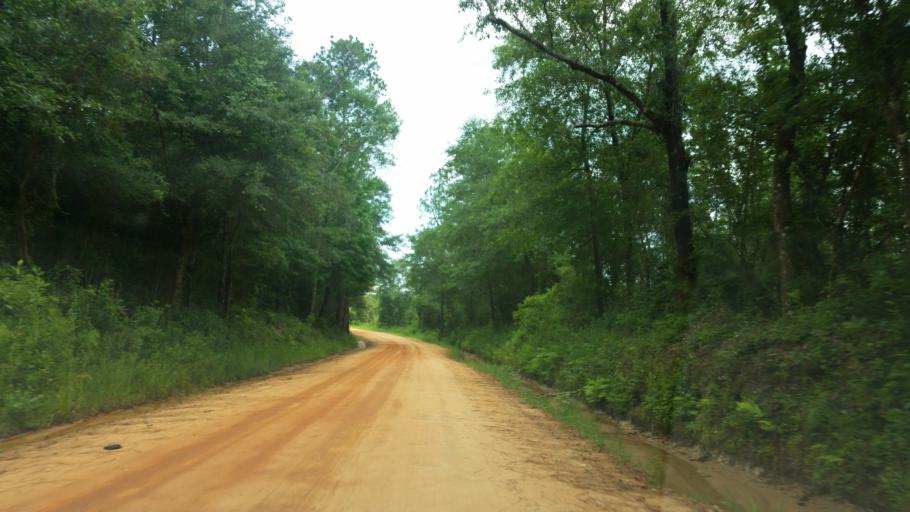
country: US
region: Florida
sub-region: Escambia County
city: Cantonment
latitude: 30.6062
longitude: -87.3948
